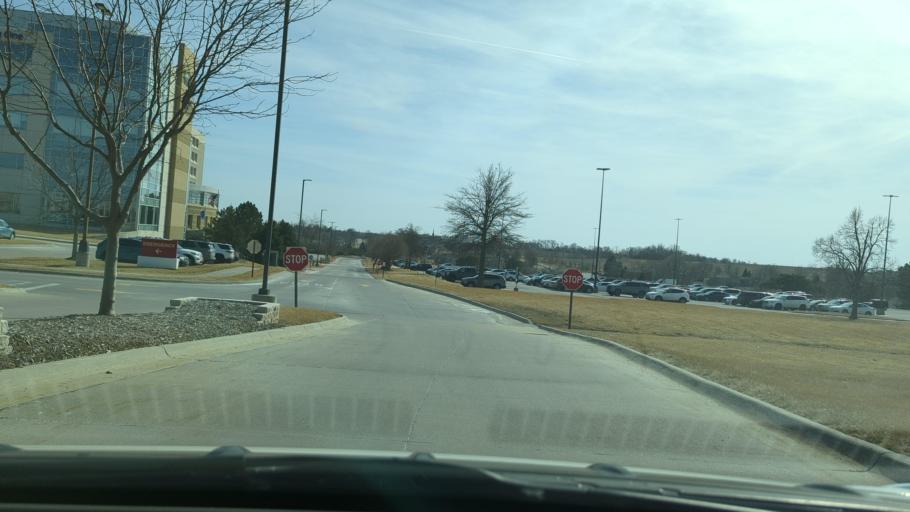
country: US
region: Nebraska
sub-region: Sarpy County
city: Papillion
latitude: 41.1373
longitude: -96.0411
